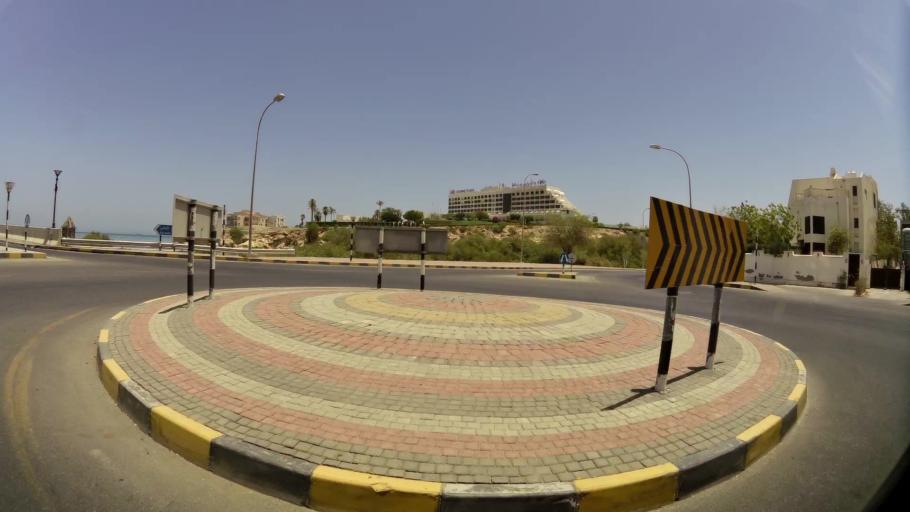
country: OM
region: Muhafazat Masqat
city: Bawshar
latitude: 23.6258
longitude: 58.4827
